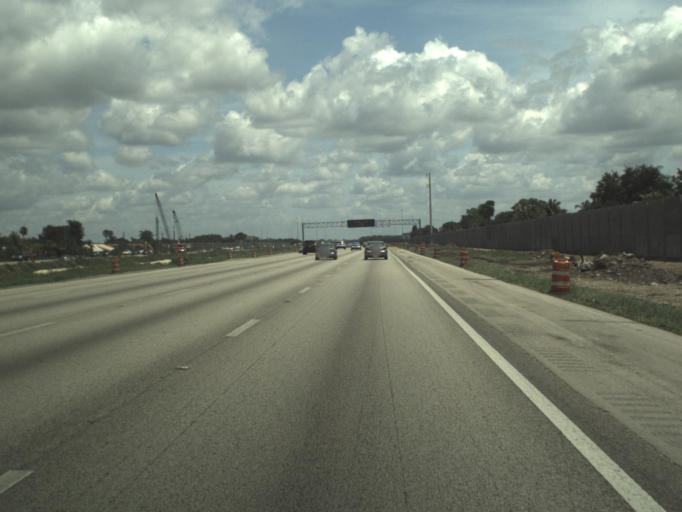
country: US
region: Florida
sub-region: Broward County
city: Southwest Ranches
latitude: 26.0460
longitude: -80.3525
